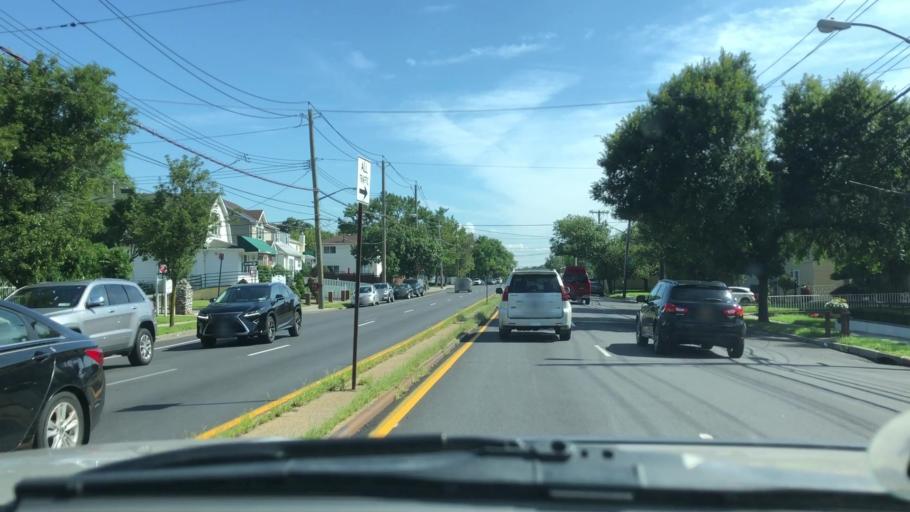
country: US
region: New York
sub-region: Richmond County
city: Staten Island
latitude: 40.5345
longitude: -74.1537
